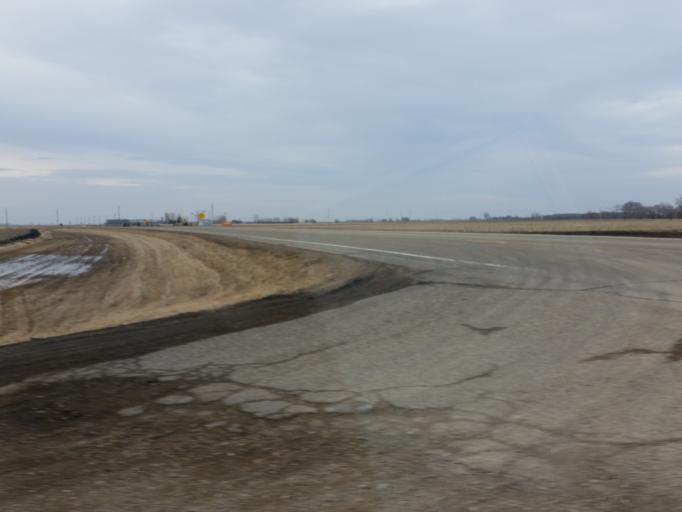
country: US
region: North Dakota
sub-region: Cass County
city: Casselton
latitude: 47.0023
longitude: -97.2143
